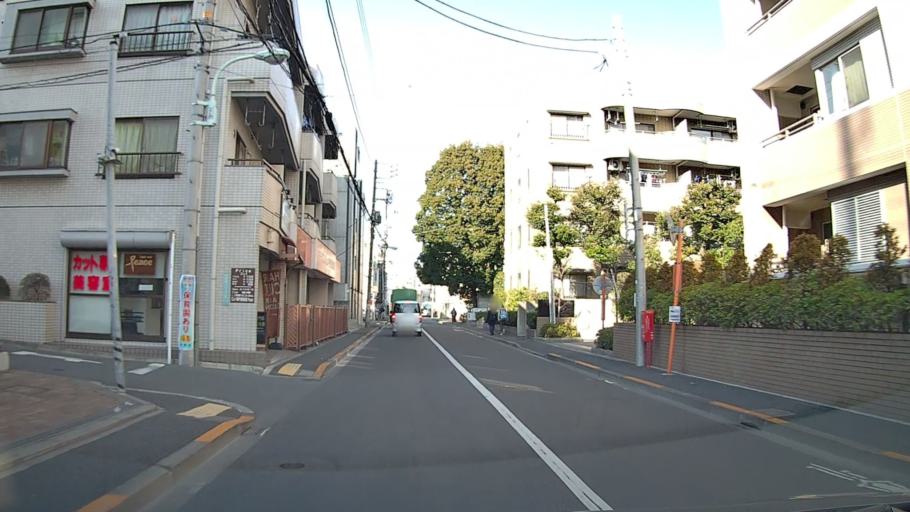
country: JP
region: Tokyo
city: Tokyo
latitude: 35.7178
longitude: 139.6362
